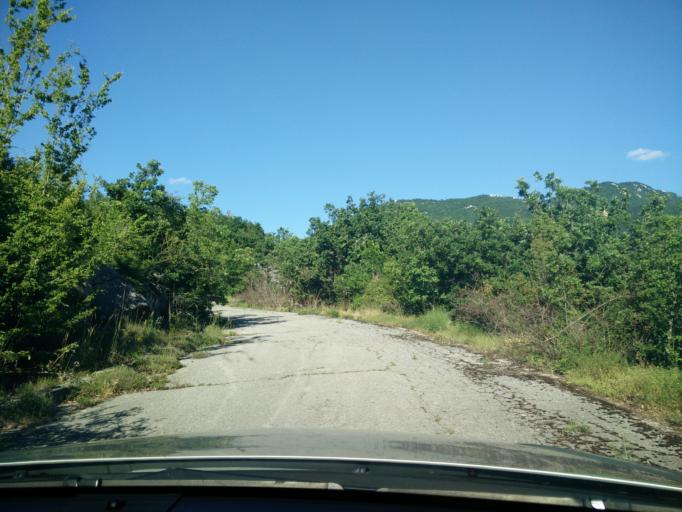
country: HR
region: Zadarska
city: Gracac
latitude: 44.4550
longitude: 15.6795
